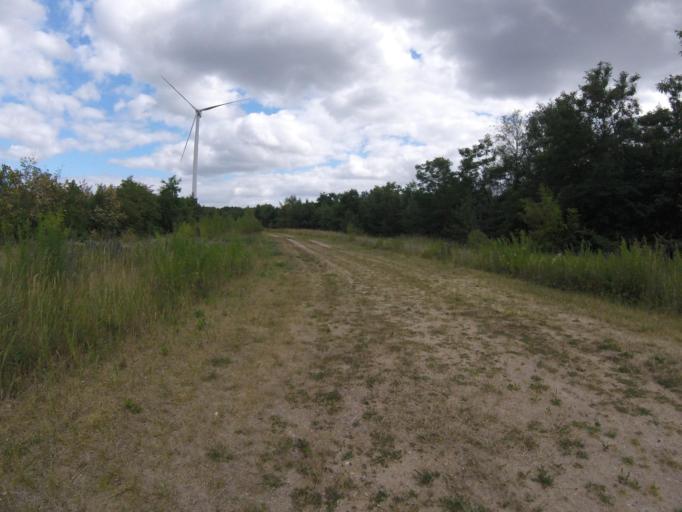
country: DE
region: Brandenburg
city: Wildau
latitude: 52.3252
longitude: 13.6789
